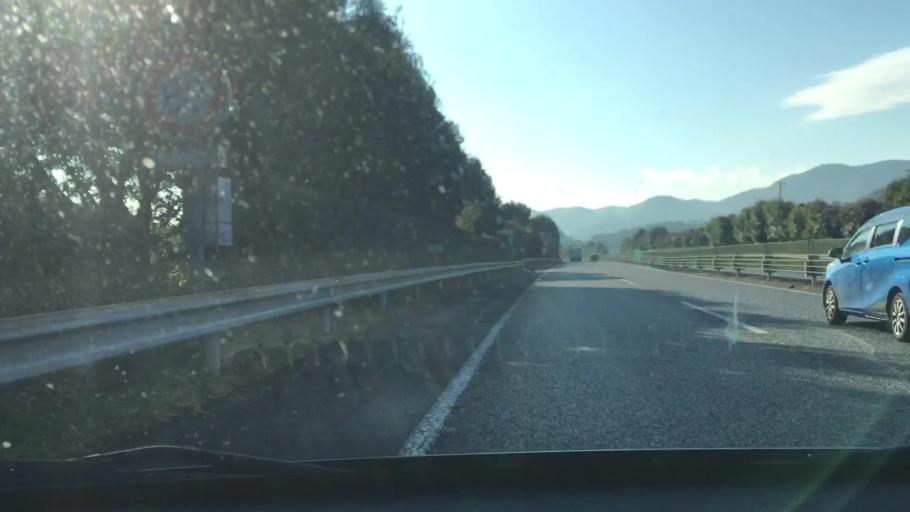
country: JP
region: Kagoshima
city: Okuchi-shinohara
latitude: 32.0161
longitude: 130.7660
